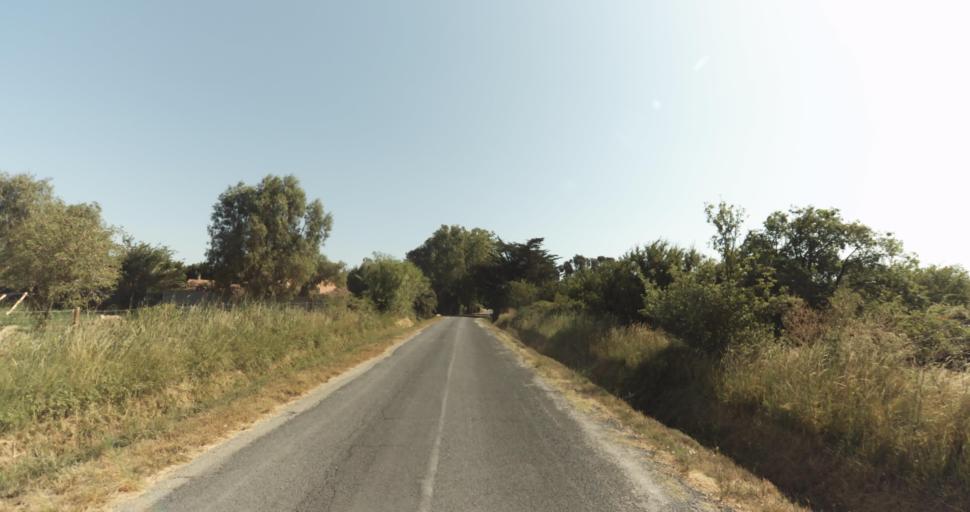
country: FR
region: Languedoc-Roussillon
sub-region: Departement des Pyrenees-Orientales
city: Saint-Cyprien-Plage
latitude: 42.6198
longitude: 3.0208
